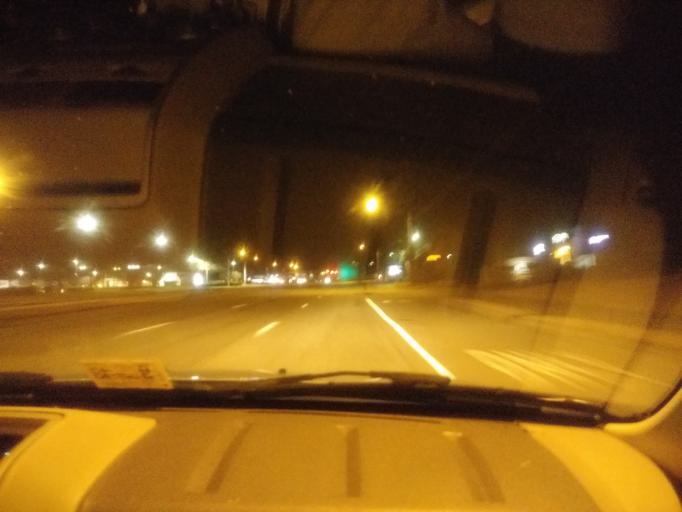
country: US
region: Virginia
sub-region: City of Chesapeake
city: Chesapeake
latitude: 36.7661
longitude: -76.2040
